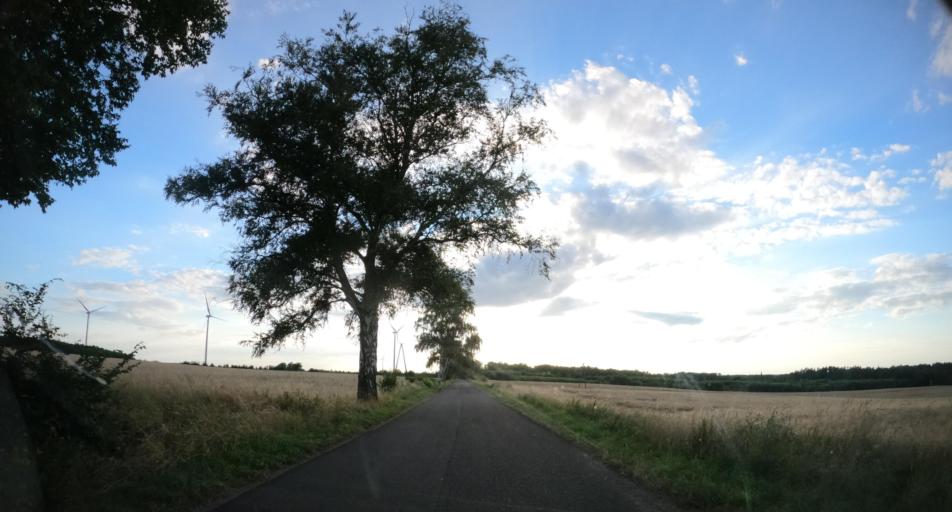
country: PL
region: West Pomeranian Voivodeship
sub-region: Powiat lobeski
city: Resko
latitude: 53.7563
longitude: 15.4373
